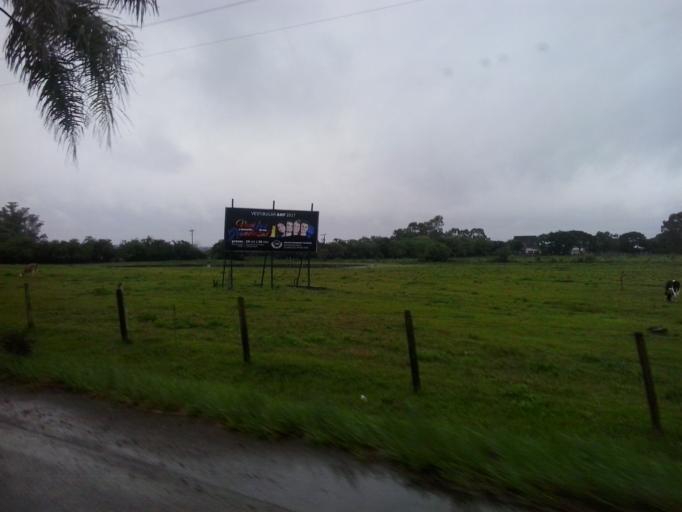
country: BR
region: Rio Grande do Sul
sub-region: Candelaria
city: Candelaria
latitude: -29.7334
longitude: -53.1801
